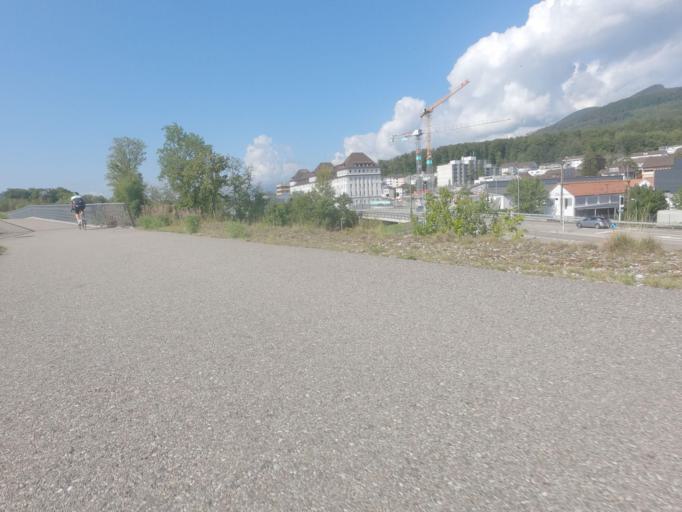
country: CH
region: Solothurn
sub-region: Bezirk Olten
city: Olten
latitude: 47.3483
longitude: 7.8928
